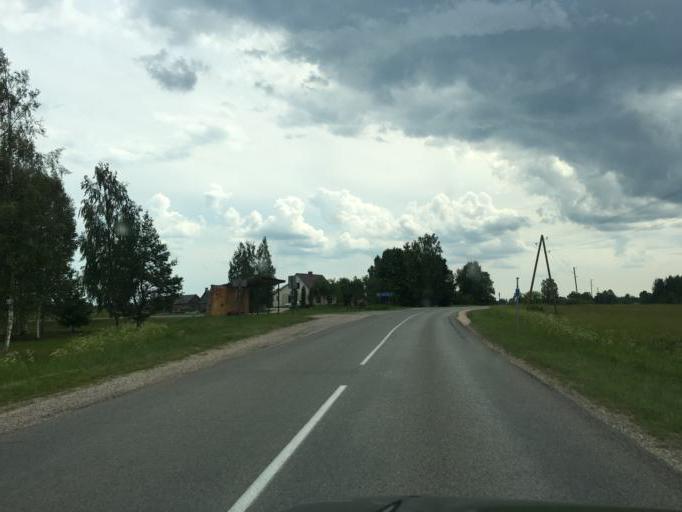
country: LV
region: Rugaju
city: Rugaji
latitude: 56.9192
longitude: 27.0715
